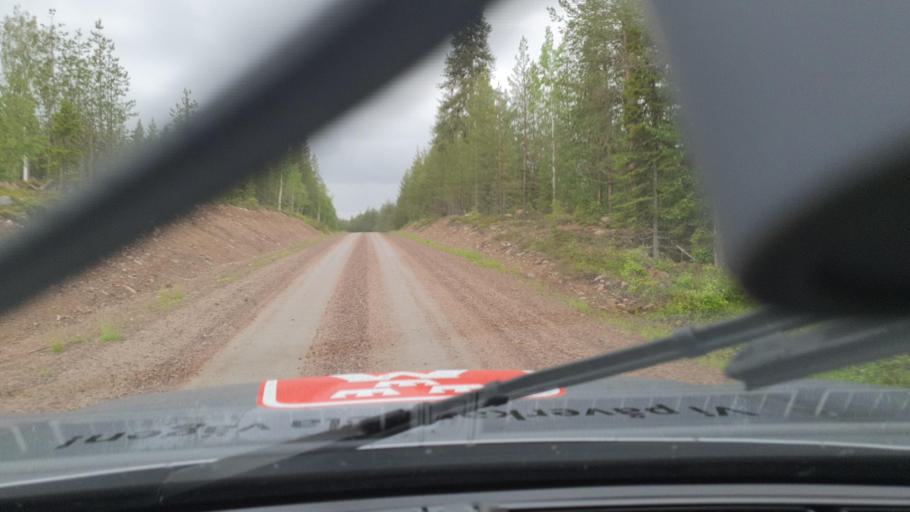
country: SE
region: Norrbotten
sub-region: Overkalix Kommun
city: OEverkalix
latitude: 66.6330
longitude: 22.7152
